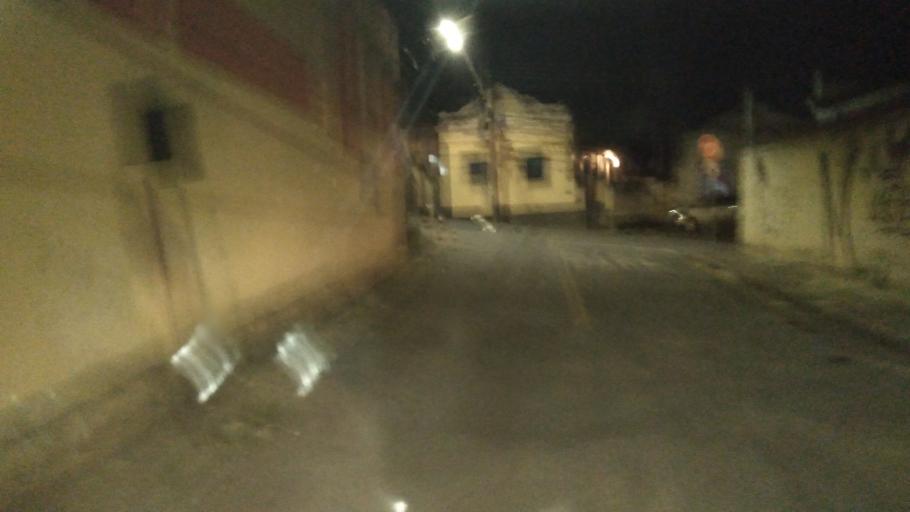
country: BR
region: Minas Gerais
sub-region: Belo Horizonte
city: Belo Horizonte
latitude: -19.9107
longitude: -43.9444
